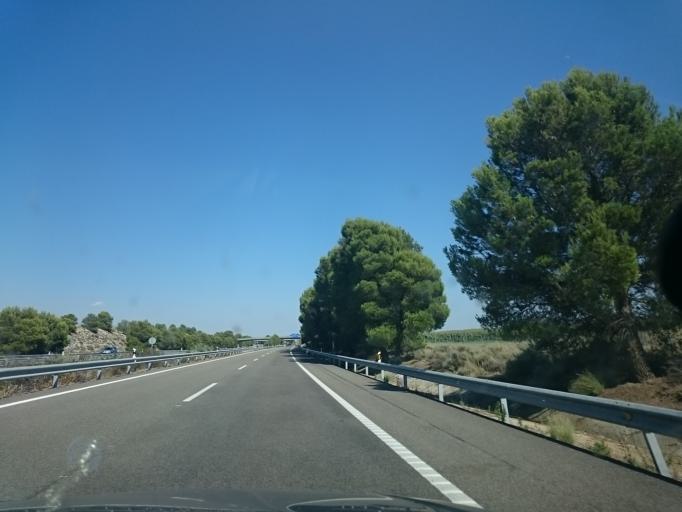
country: ES
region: Aragon
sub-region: Provincia de Zaragoza
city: Bujaraloz
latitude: 41.5258
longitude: -0.1893
